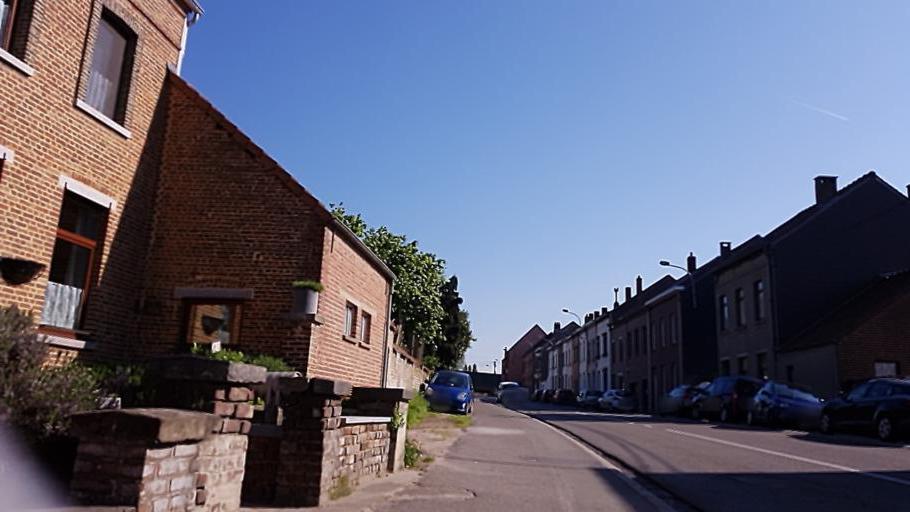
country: BE
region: Wallonia
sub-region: Province du Brabant Wallon
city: Wavre
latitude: 50.7104
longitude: 4.5975
